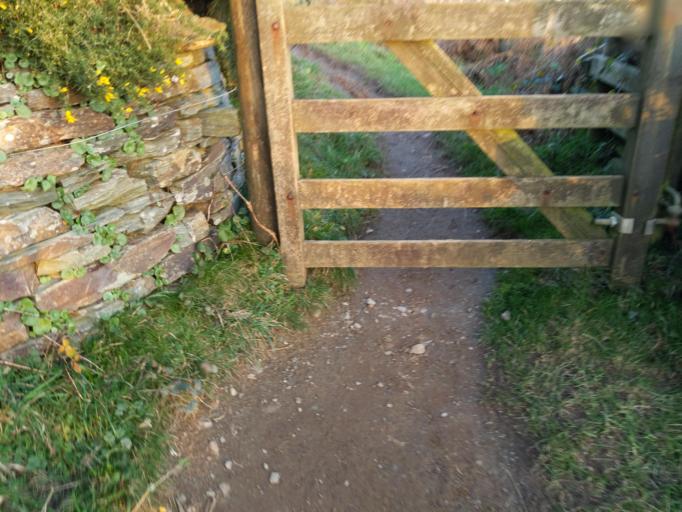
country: GB
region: England
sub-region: Cornwall
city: Fowey
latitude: 50.3290
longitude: -4.6092
